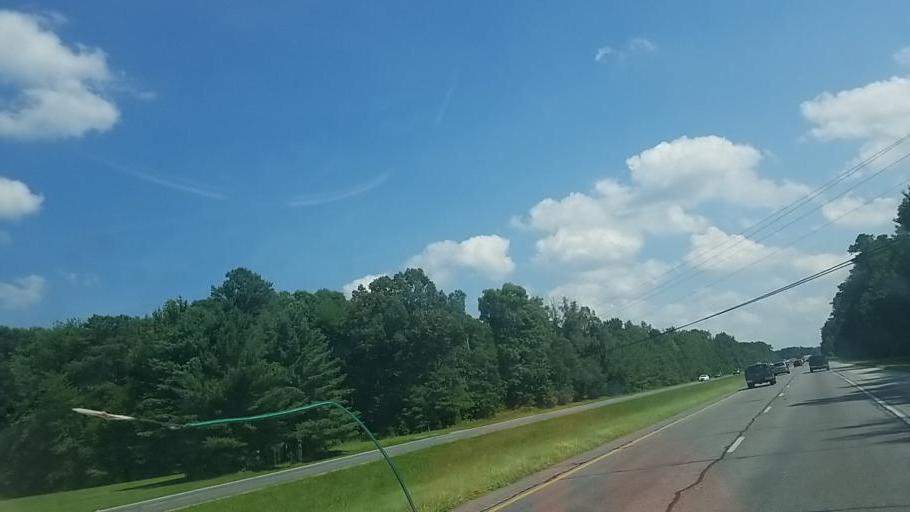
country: US
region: Delaware
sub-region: Sussex County
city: Georgetown
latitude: 38.7332
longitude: -75.4194
